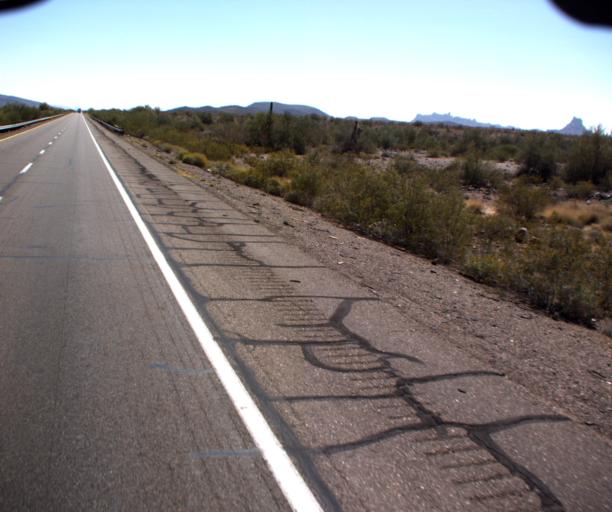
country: US
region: Arizona
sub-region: La Paz County
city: Quartzsite
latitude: 33.6590
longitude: -113.9907
